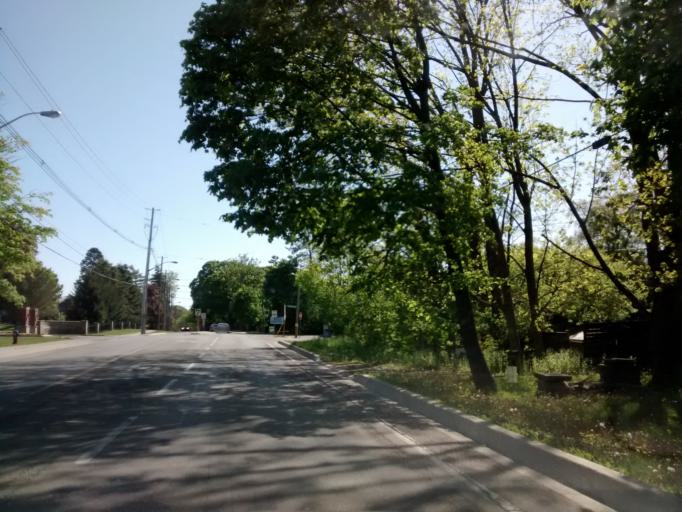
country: CA
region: Ontario
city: Oakville
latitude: 43.4287
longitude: -79.6866
